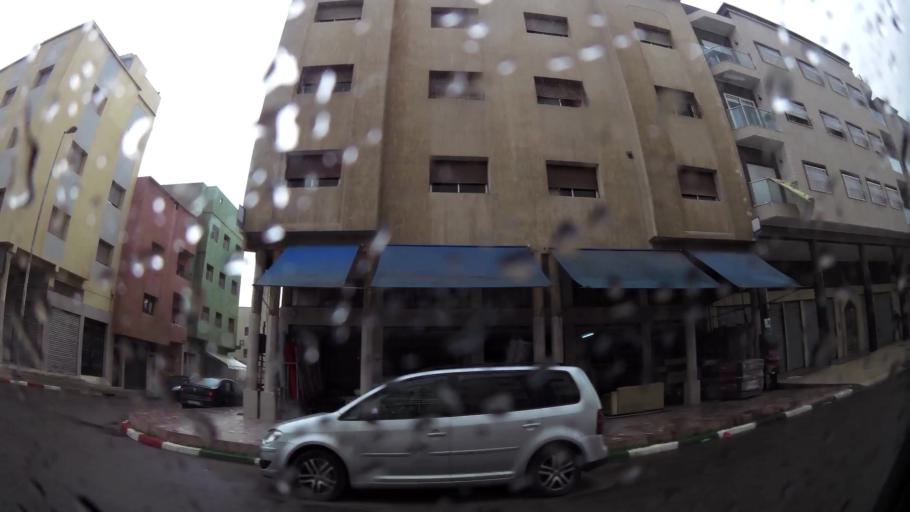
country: MA
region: Grand Casablanca
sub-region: Mediouna
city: Tit Mellil
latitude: 33.6224
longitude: -7.4831
